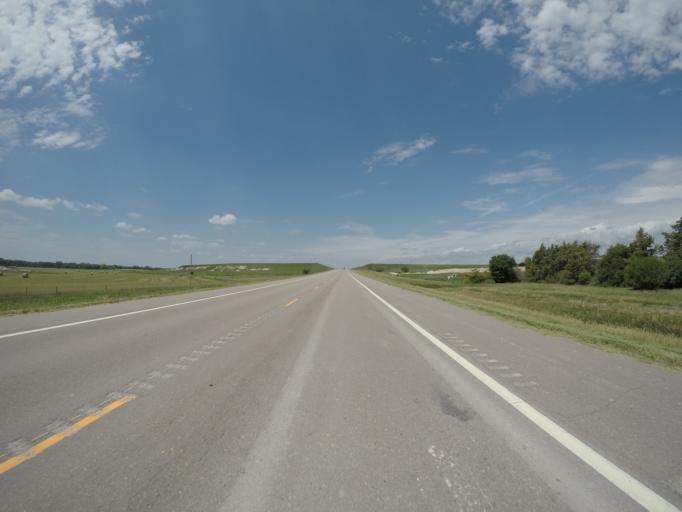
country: US
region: Kansas
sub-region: Graham County
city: Hill City
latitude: 39.3795
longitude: -99.6974
